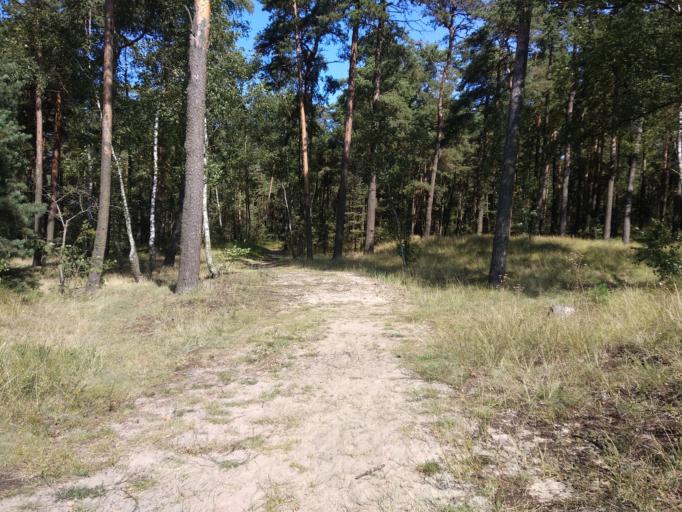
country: LT
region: Klaipedos apskritis
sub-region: Klaipeda
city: Klaipeda
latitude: 55.7287
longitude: 21.1101
